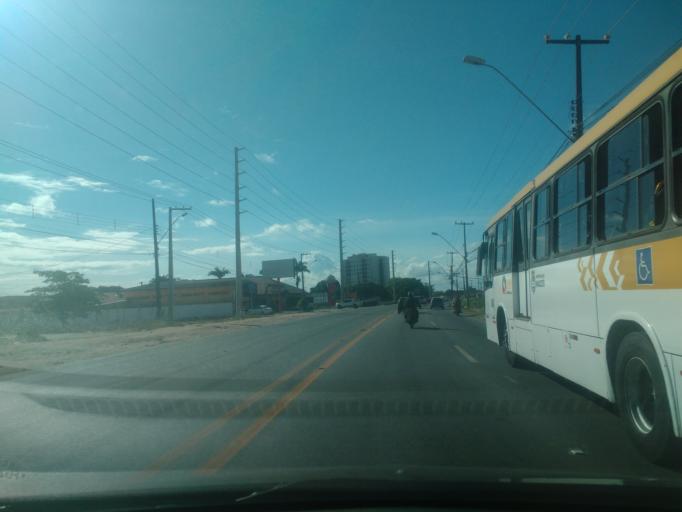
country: BR
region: Alagoas
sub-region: Satuba
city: Satuba
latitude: -9.5707
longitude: -35.7418
